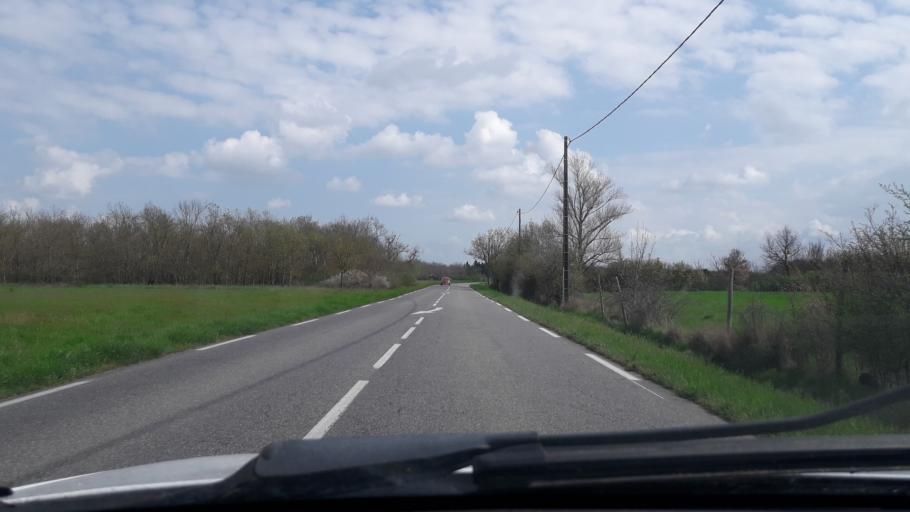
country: FR
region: Midi-Pyrenees
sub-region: Departement de la Haute-Garonne
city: Seysses
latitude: 43.5030
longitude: 1.2646
